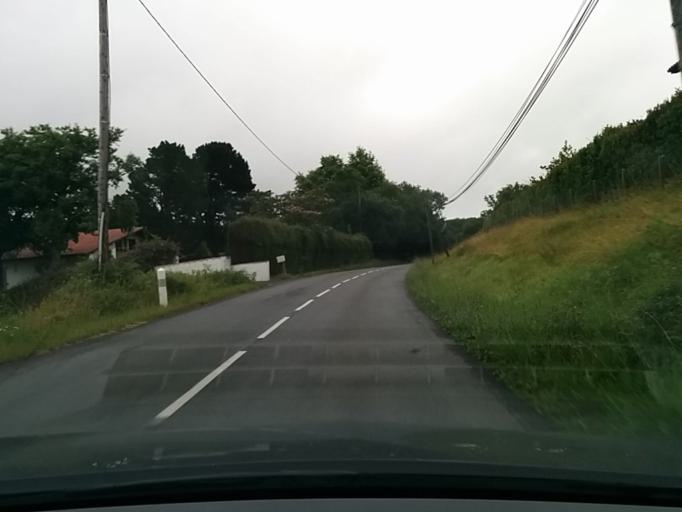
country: FR
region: Aquitaine
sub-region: Departement des Pyrenees-Atlantiques
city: Ascain
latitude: 43.3806
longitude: -1.6081
